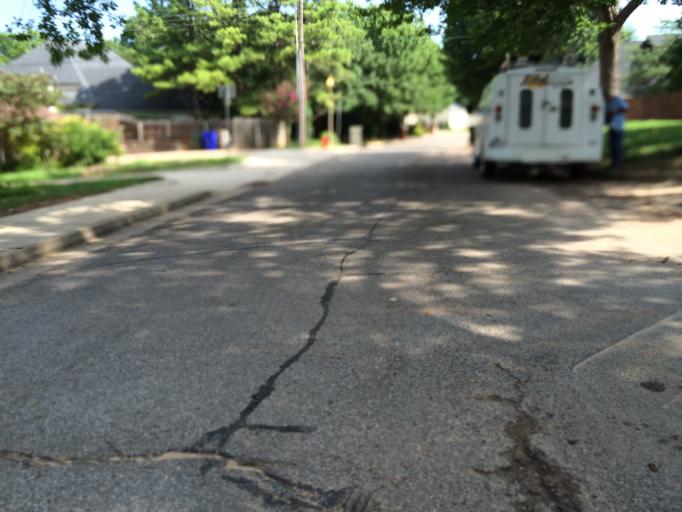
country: US
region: Oklahoma
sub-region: Cleveland County
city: Norman
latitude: 35.2009
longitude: -97.4568
